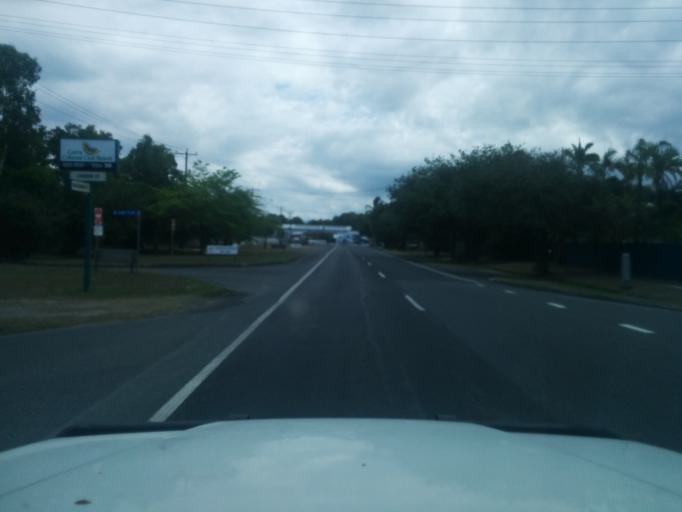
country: AU
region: Queensland
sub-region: Cairns
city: Cairns
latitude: -16.9121
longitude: 145.7500
